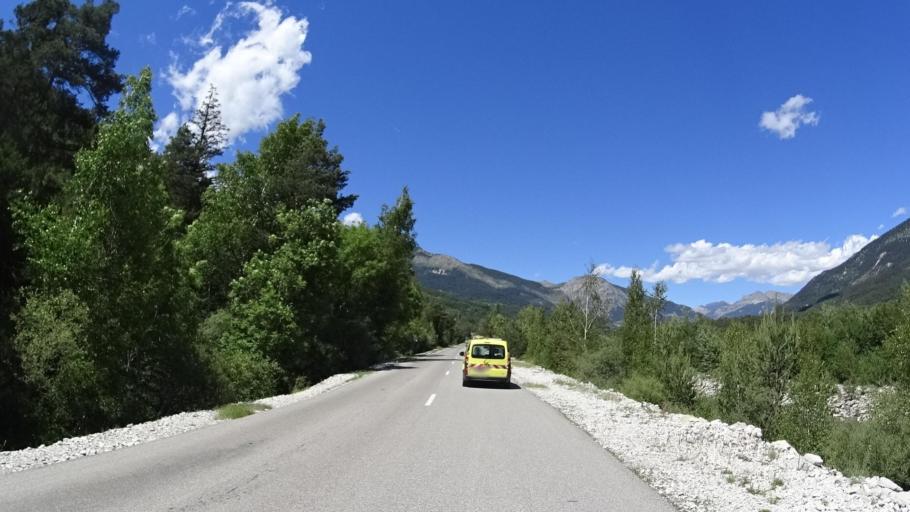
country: FR
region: Provence-Alpes-Cote d'Azur
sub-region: Departement des Alpes-de-Haute-Provence
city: Annot
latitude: 44.1221
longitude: 6.5805
